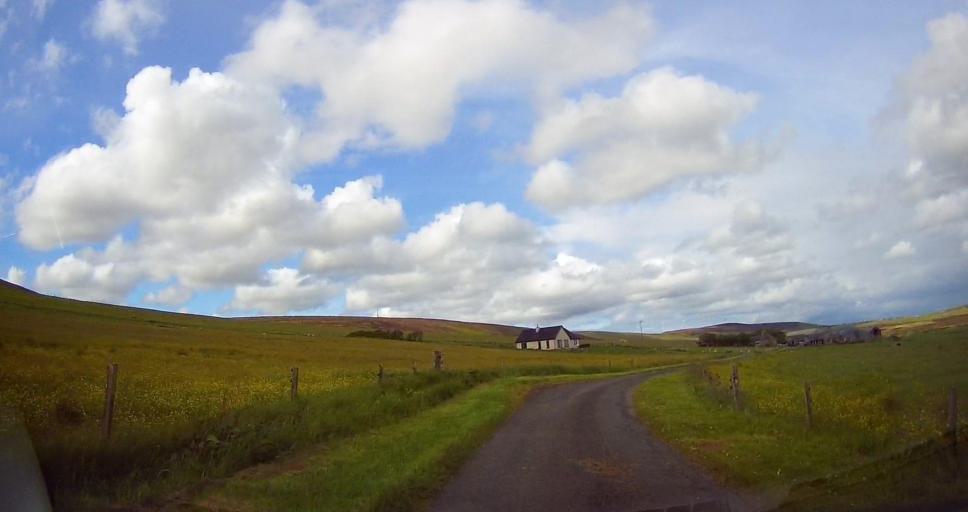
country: GB
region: Scotland
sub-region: Orkney Islands
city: Orkney
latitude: 59.0546
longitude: -3.1038
